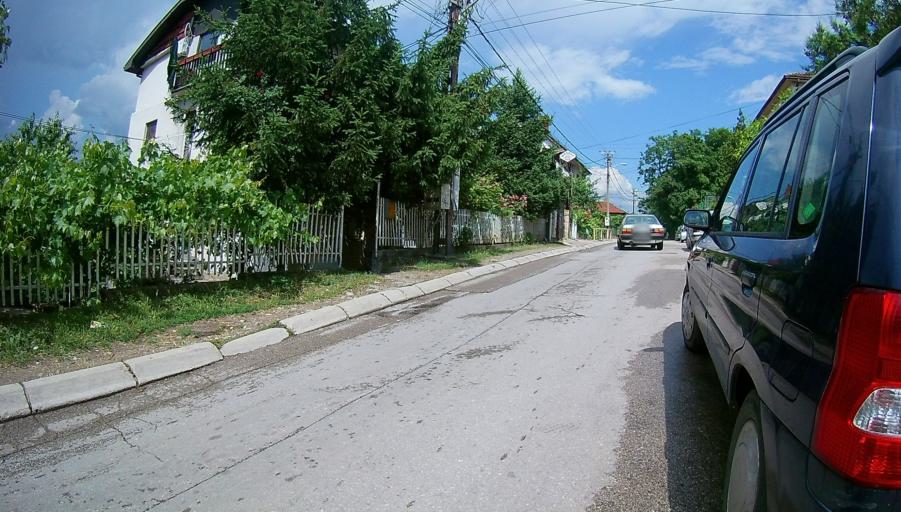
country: RS
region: Central Serbia
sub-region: Nisavski Okrug
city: Nis
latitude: 43.3089
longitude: 21.8991
